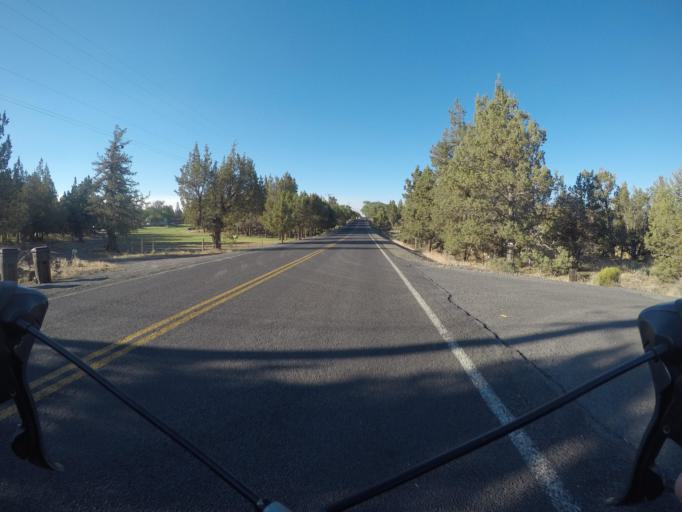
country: US
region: Oregon
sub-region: Deschutes County
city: Redmond
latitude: 44.2513
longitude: -121.2396
